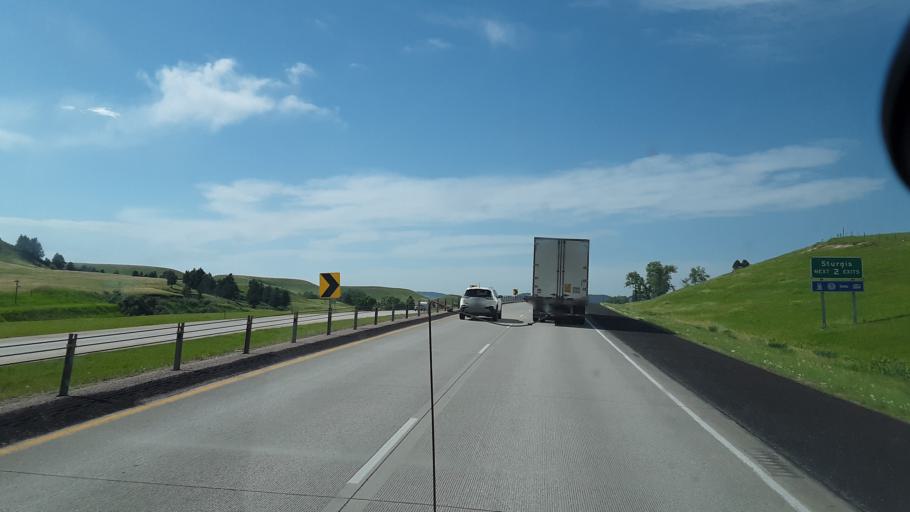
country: US
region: South Dakota
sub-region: Meade County
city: Sturgis
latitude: 44.3792
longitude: -103.4817
